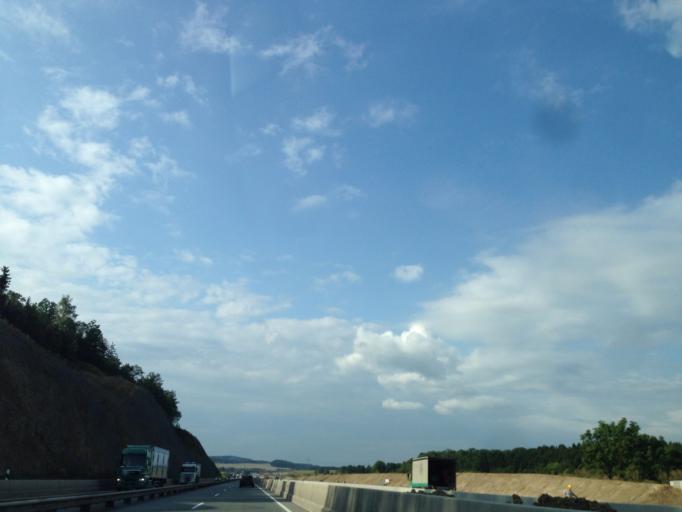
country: DE
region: Thuringia
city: Gorkwitz
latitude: 50.5956
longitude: 11.7853
